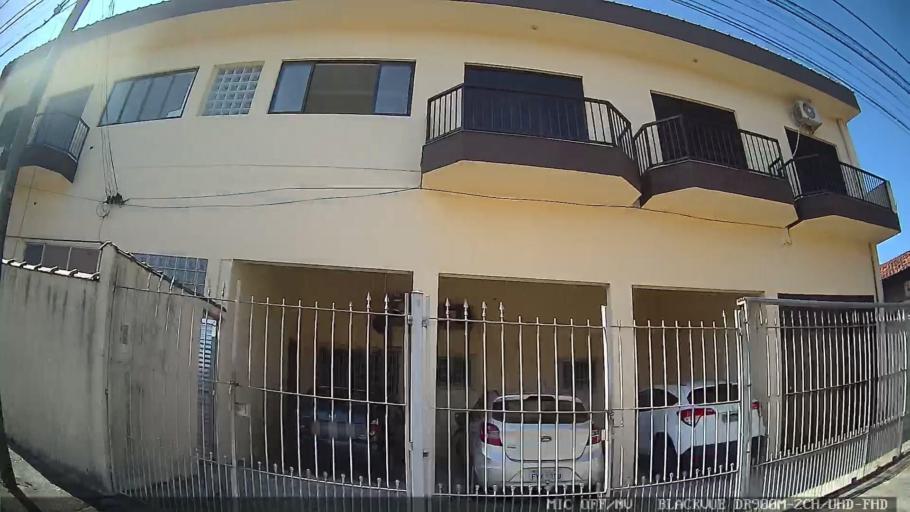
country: BR
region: Sao Paulo
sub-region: Peruibe
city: Peruibe
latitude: -24.2765
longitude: -46.9446
